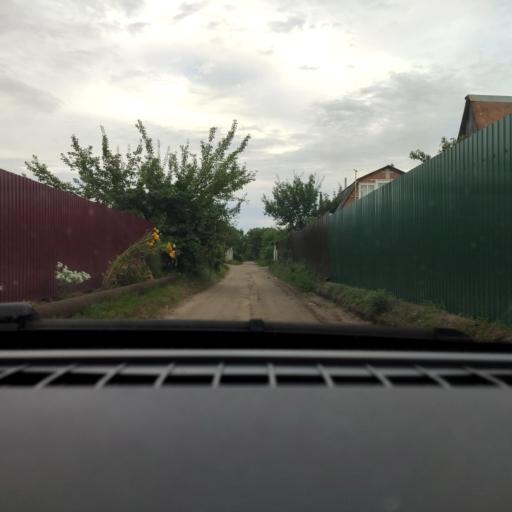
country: RU
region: Voronezj
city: Maslovka
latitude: 51.5221
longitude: 39.2345
